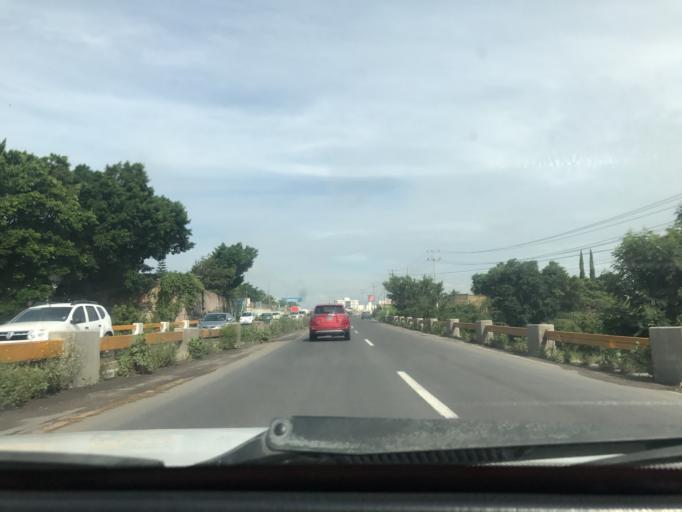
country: MX
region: Morelos
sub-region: Cuautla
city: Tierra Larga (Campo Nuevo)
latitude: 18.8473
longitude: -98.9320
